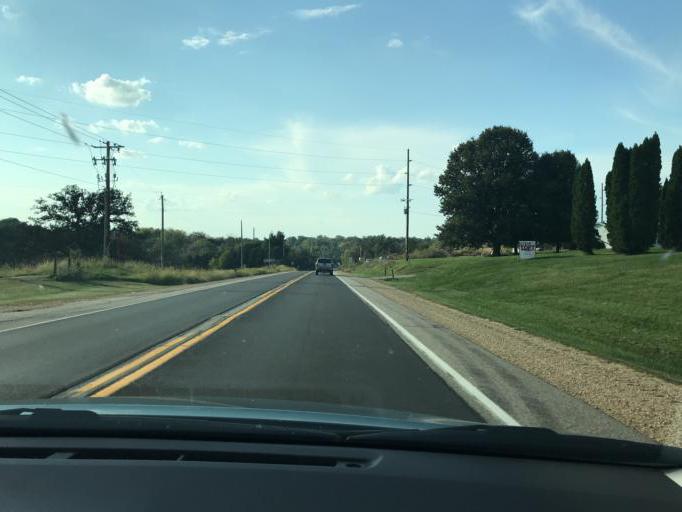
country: US
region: Wisconsin
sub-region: Grant County
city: Platteville
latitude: 42.7220
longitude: -90.4696
